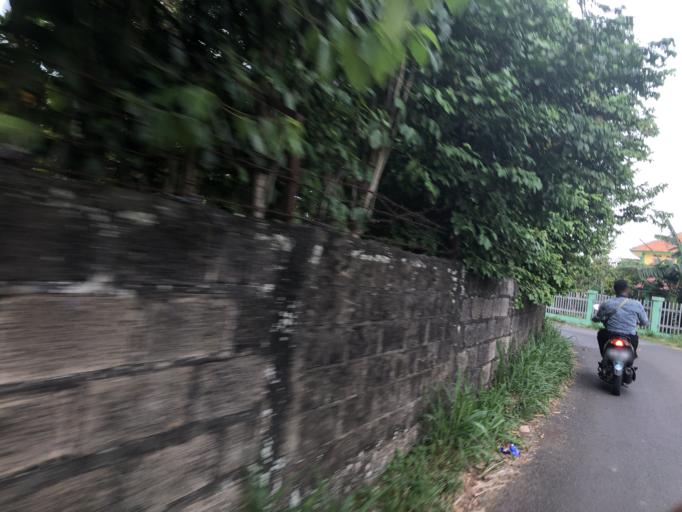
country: ID
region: West Java
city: Ciampea
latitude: -6.5649
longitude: 106.7455
